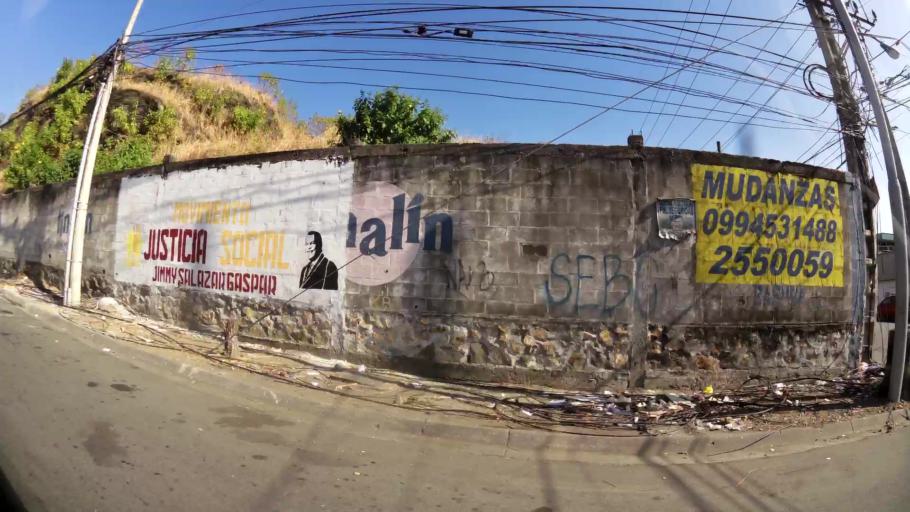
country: EC
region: Guayas
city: Eloy Alfaro
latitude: -2.1562
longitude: -79.8977
